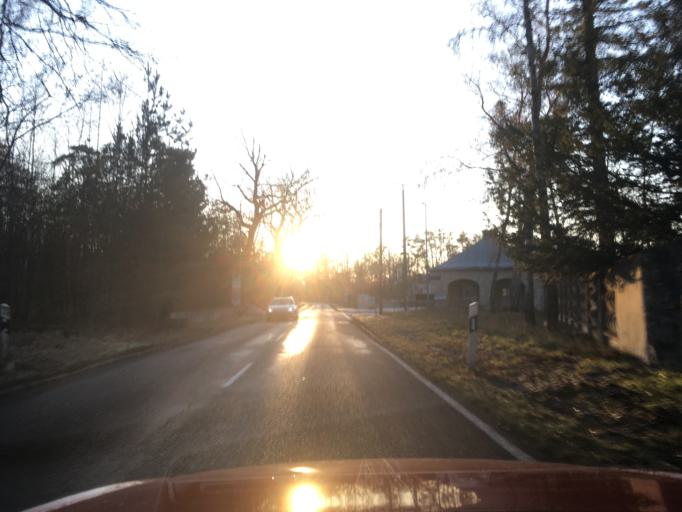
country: DE
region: Saxony-Anhalt
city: Rosslau
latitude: 51.8977
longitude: 12.2701
